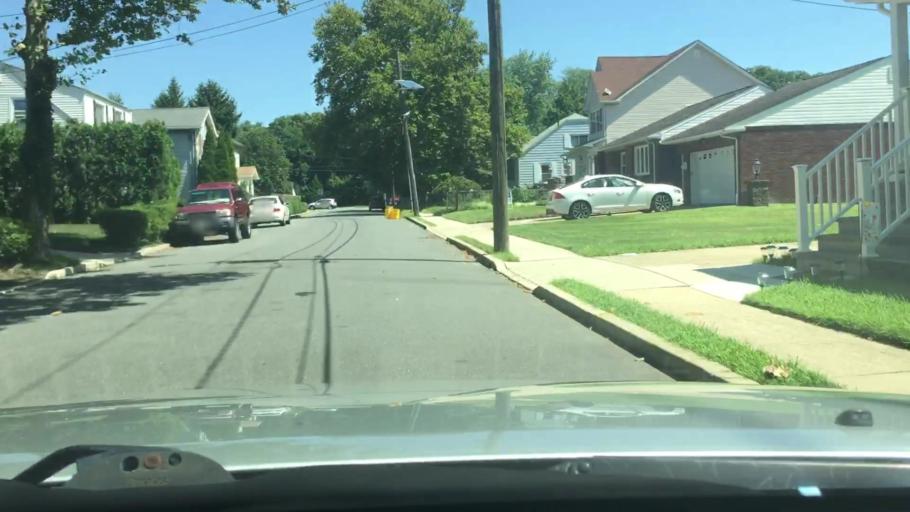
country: US
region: New Jersey
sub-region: Middlesex County
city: South River
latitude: 40.4546
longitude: -74.3950
